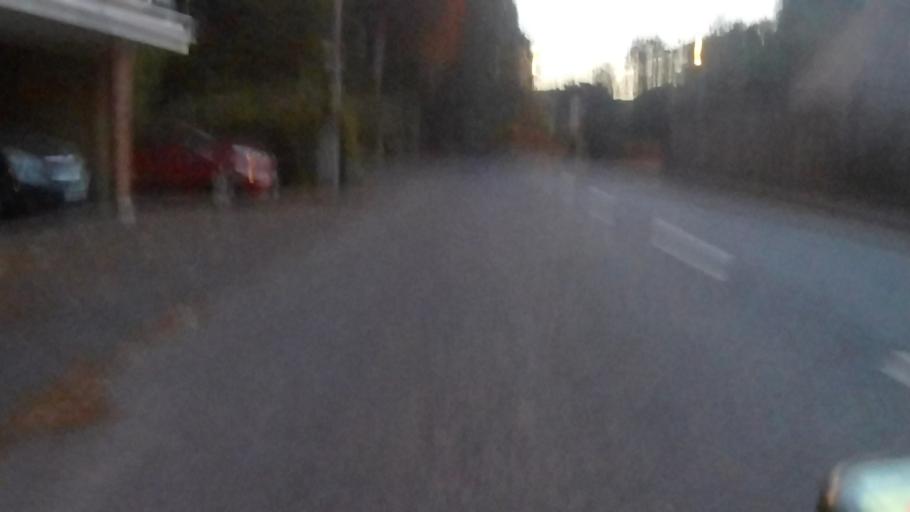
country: IE
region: Munster
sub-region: County Cork
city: Passage West
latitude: 51.9285
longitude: -8.3913
